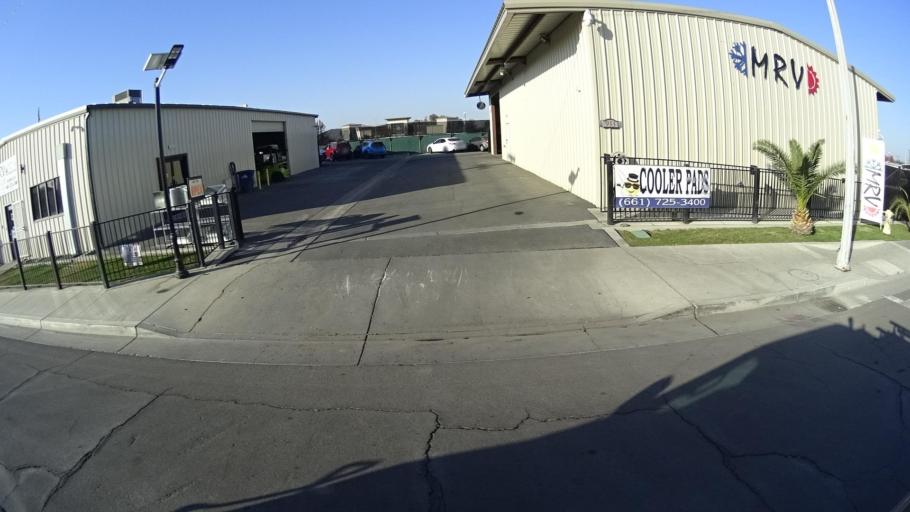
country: US
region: California
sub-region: Kern County
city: Delano
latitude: 35.7688
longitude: -119.2469
